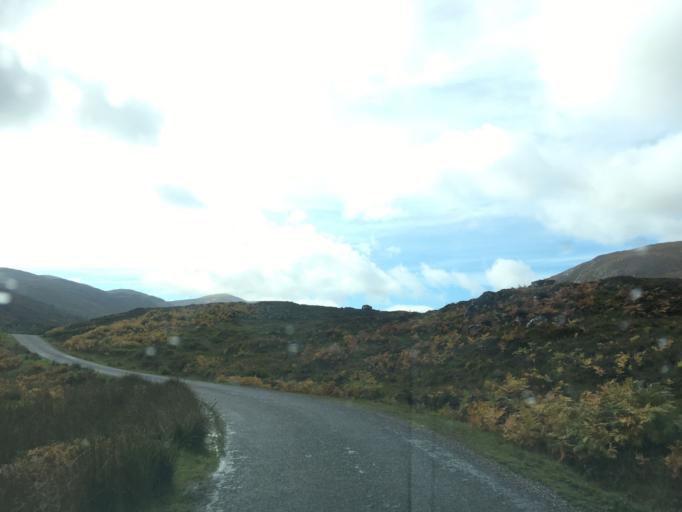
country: GB
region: Scotland
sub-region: Highland
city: Beauly
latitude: 57.3562
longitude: -4.8901
